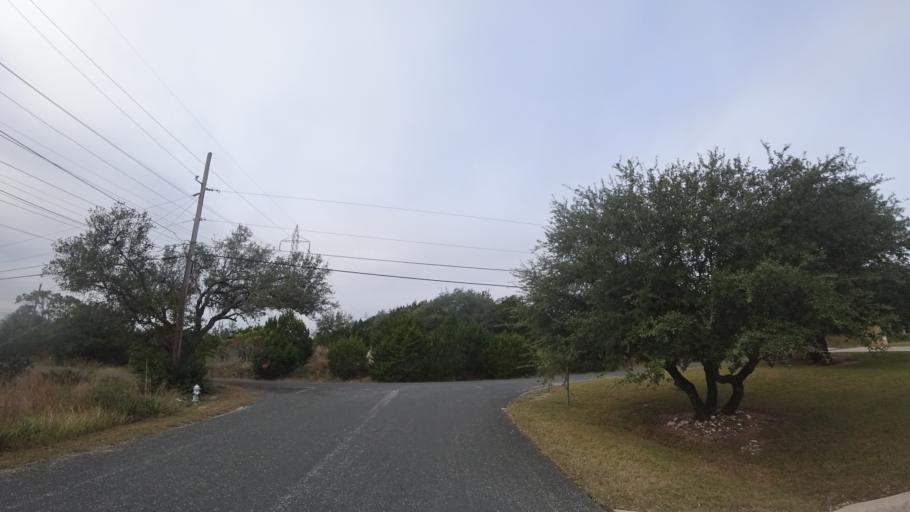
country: US
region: Texas
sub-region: Travis County
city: Hudson Bend
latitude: 30.3921
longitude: -97.9148
